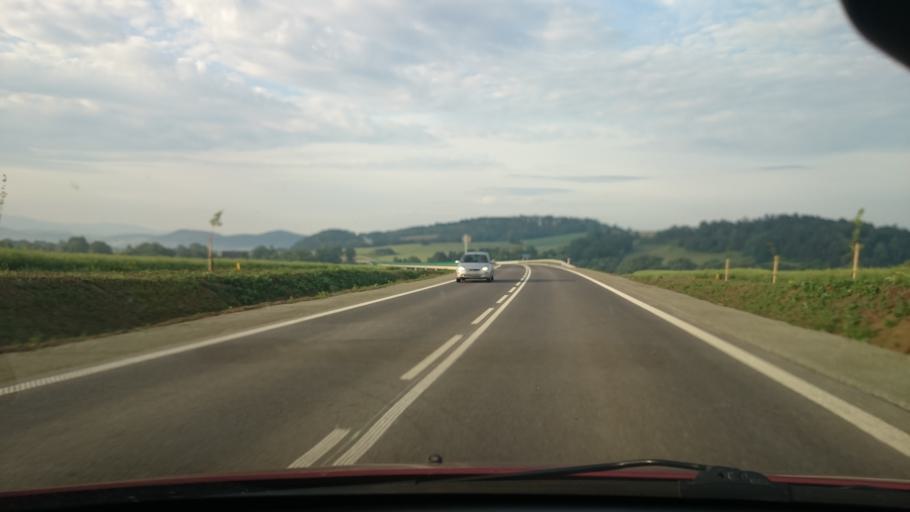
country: PL
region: Lower Silesian Voivodeship
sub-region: Powiat klodzki
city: Klodzko
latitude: 50.4194
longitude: 16.6257
